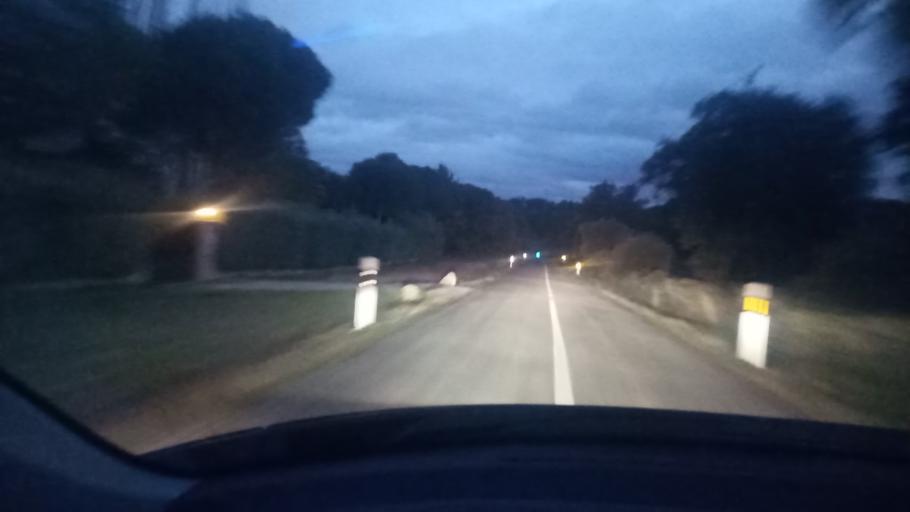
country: ES
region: Madrid
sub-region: Provincia de Madrid
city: Colmenar del Arroyo
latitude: 40.4322
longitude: -4.2244
